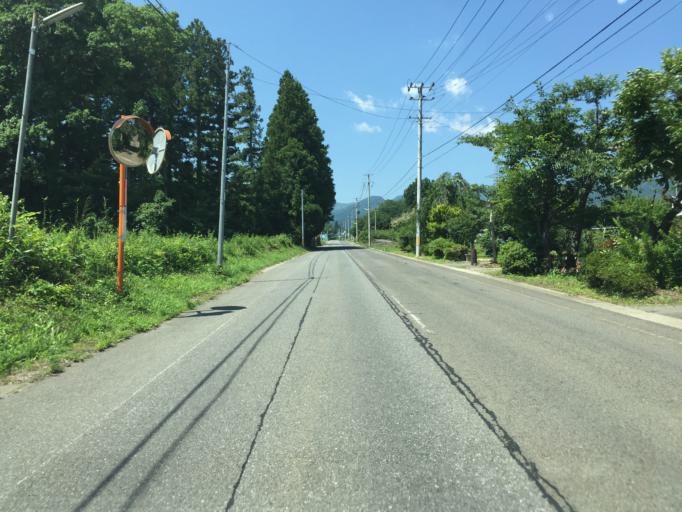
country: JP
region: Fukushima
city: Fukushima-shi
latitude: 37.7077
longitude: 140.3688
